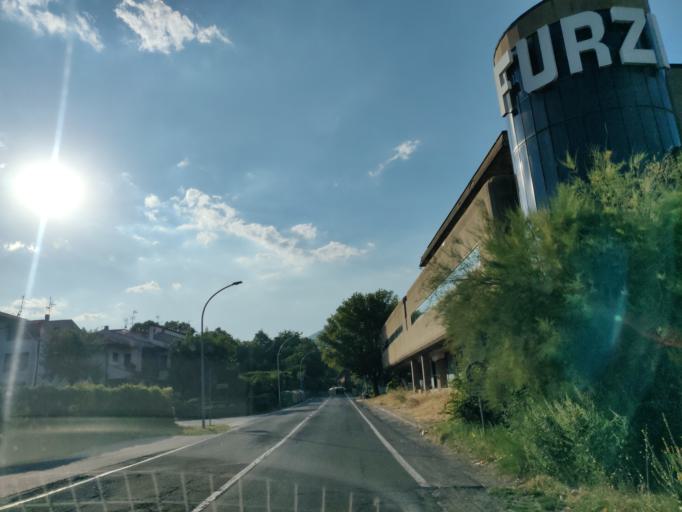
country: IT
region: Tuscany
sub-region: Provincia di Siena
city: Piancastagnaio
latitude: 42.8523
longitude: 11.6872
